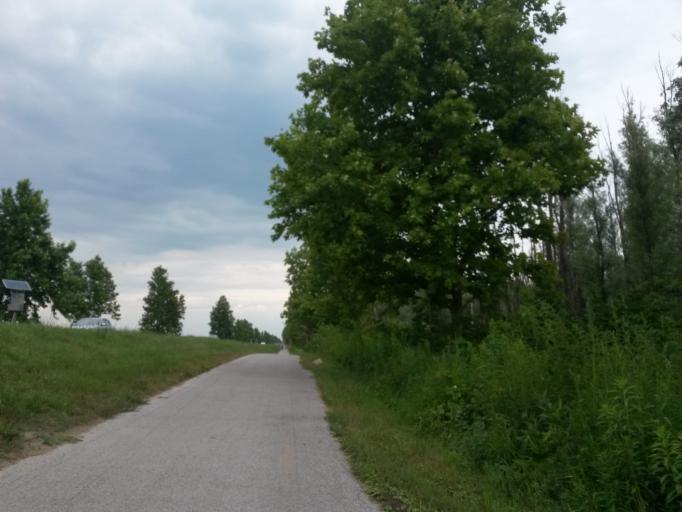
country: HR
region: Osjecko-Baranjska
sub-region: Grad Osijek
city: Bilje
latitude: 45.5796
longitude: 18.7221
